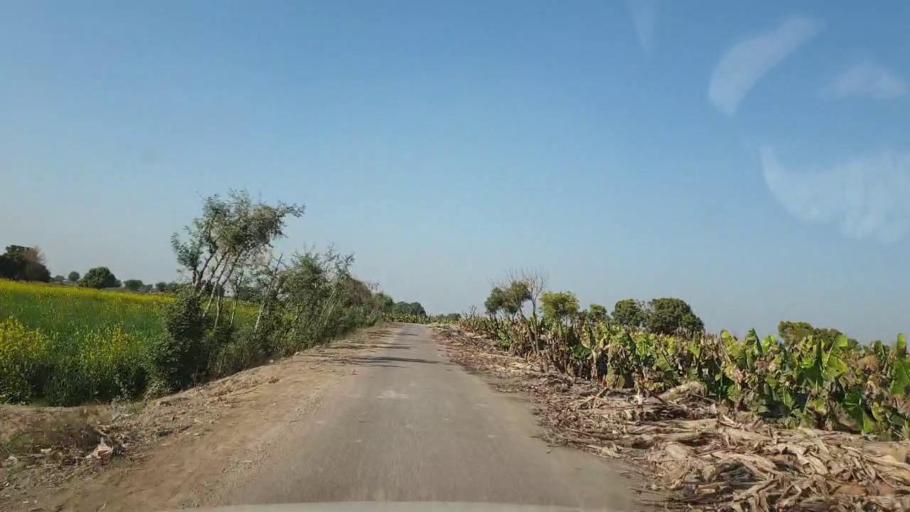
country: PK
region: Sindh
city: Tando Allahyar
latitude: 25.4779
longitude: 68.6601
